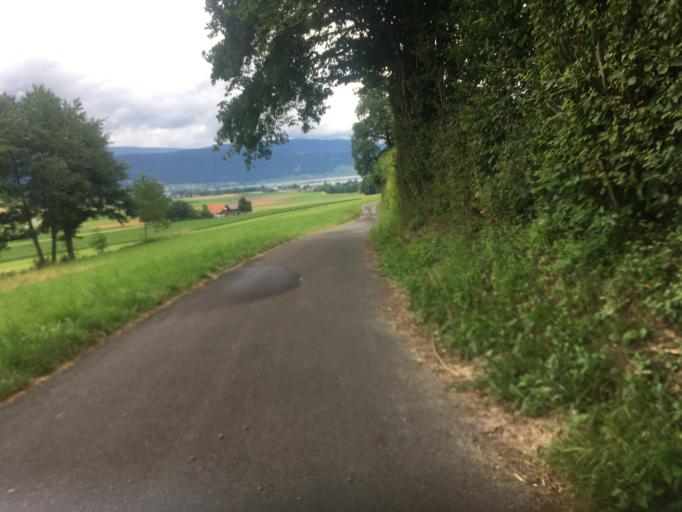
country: CH
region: Bern
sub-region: Seeland District
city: Ins
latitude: 47.0148
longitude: 7.0985
